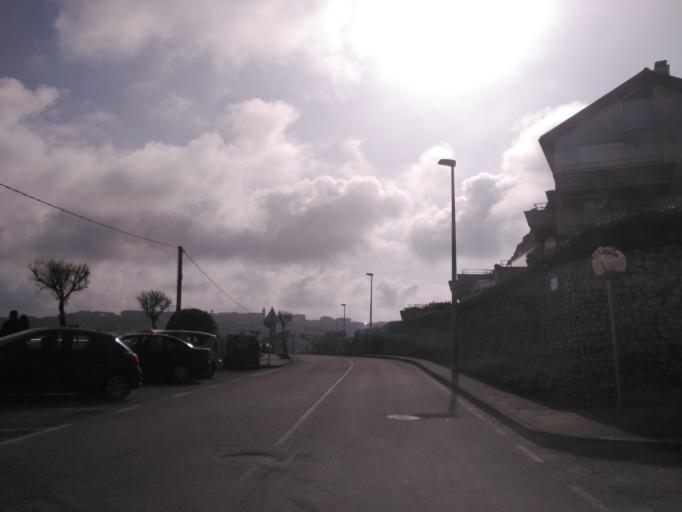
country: ES
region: Cantabria
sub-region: Provincia de Cantabria
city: Suances
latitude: 43.4375
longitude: -4.0459
